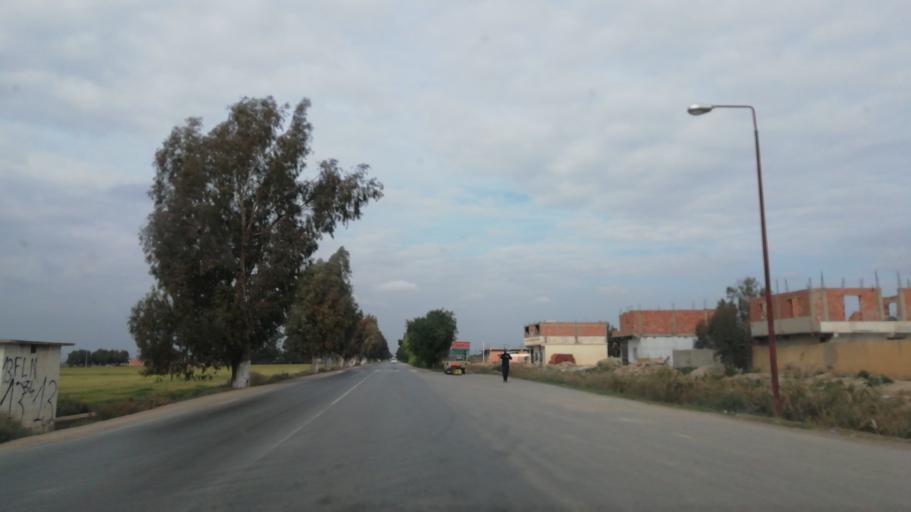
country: DZ
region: Mascara
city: Mascara
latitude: 35.6314
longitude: 0.0612
